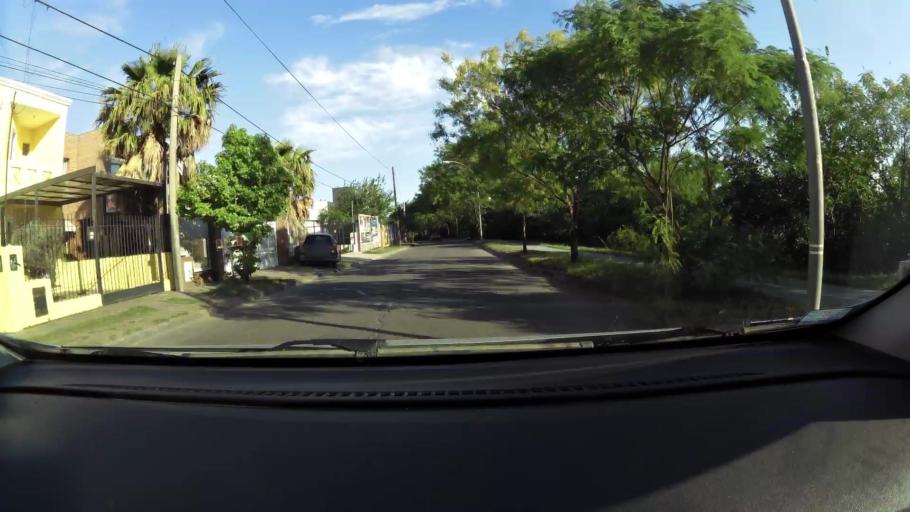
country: AR
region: Cordoba
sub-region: Departamento de Capital
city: Cordoba
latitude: -31.3863
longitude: -64.2419
